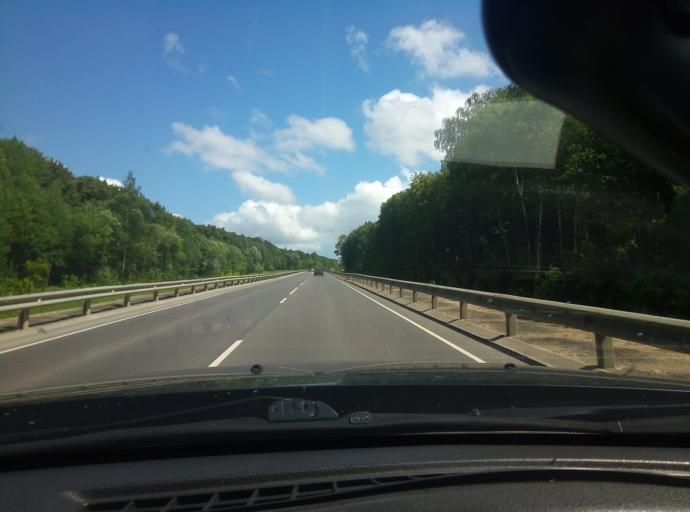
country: RU
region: Tula
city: Novogurovskiy
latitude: 54.2789
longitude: 37.2351
